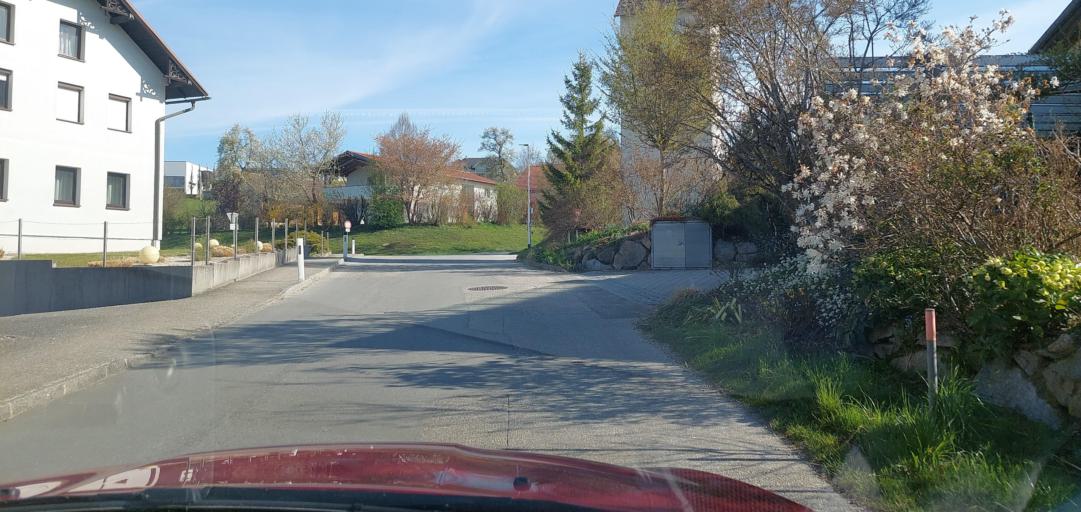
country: AT
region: Upper Austria
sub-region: Politischer Bezirk Ried im Innkreis
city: Ried im Innkreis
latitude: 48.1981
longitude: 13.5040
